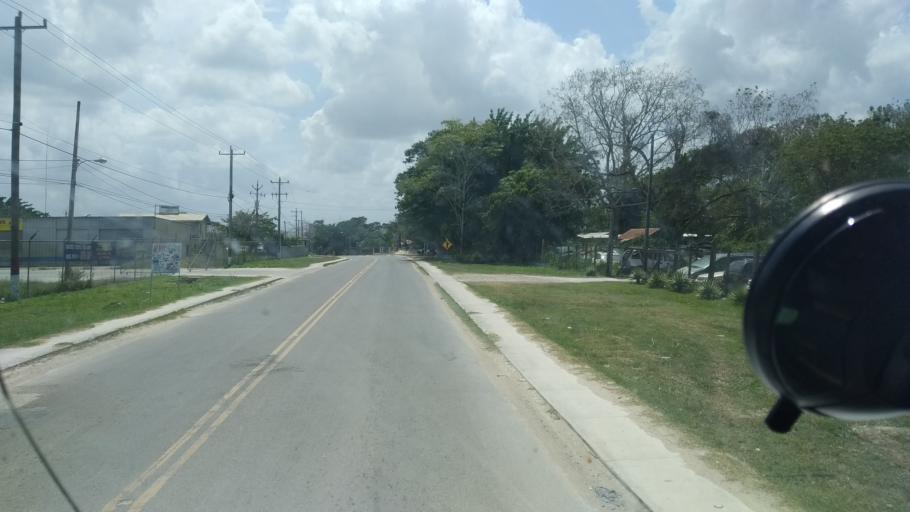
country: BZ
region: Orange Walk
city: Orange Walk
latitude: 18.0649
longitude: -88.5716
